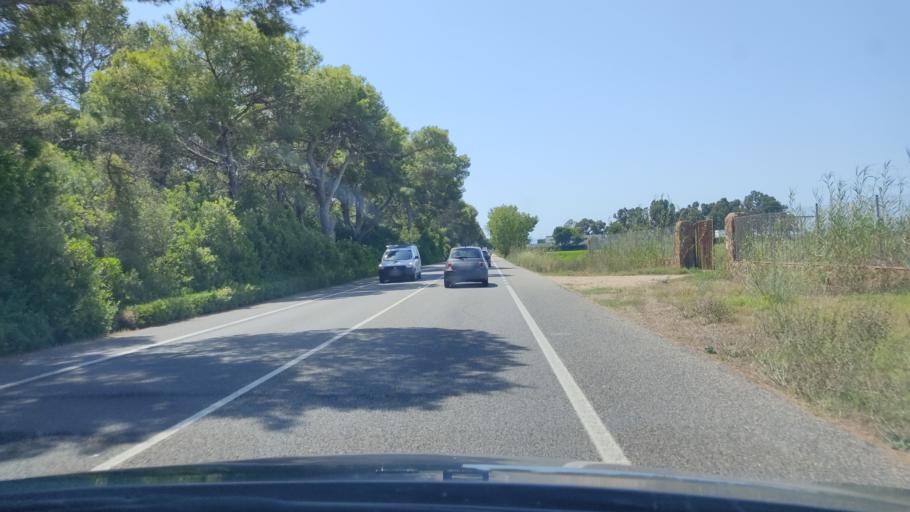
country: ES
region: Valencia
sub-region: Provincia de Valencia
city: Alfafar
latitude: 39.3648
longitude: -0.3282
